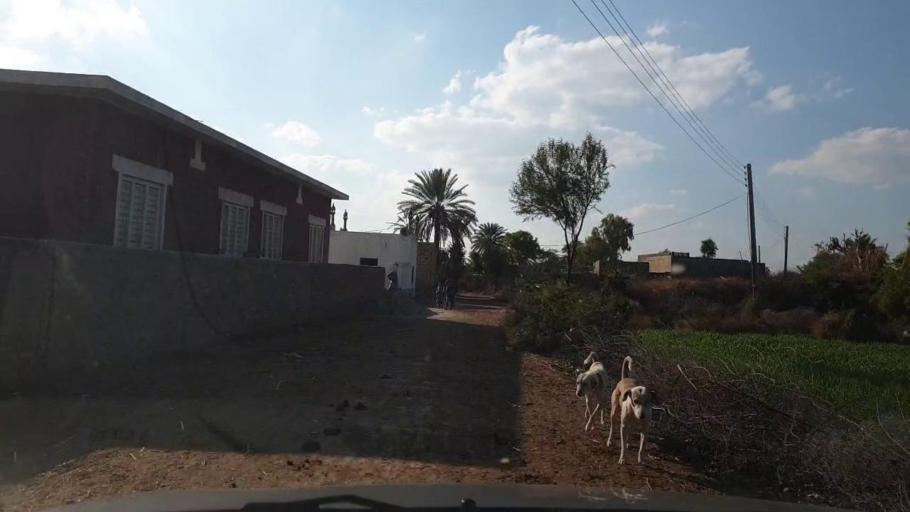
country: PK
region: Sindh
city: Sinjhoro
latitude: 25.9998
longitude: 68.7235
